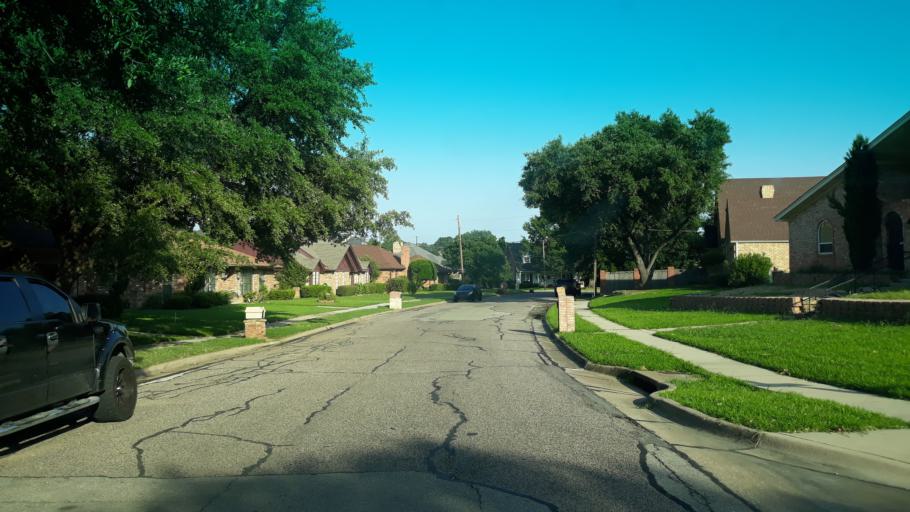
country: US
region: Texas
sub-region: Dallas County
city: Irving
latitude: 32.8539
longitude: -96.9800
